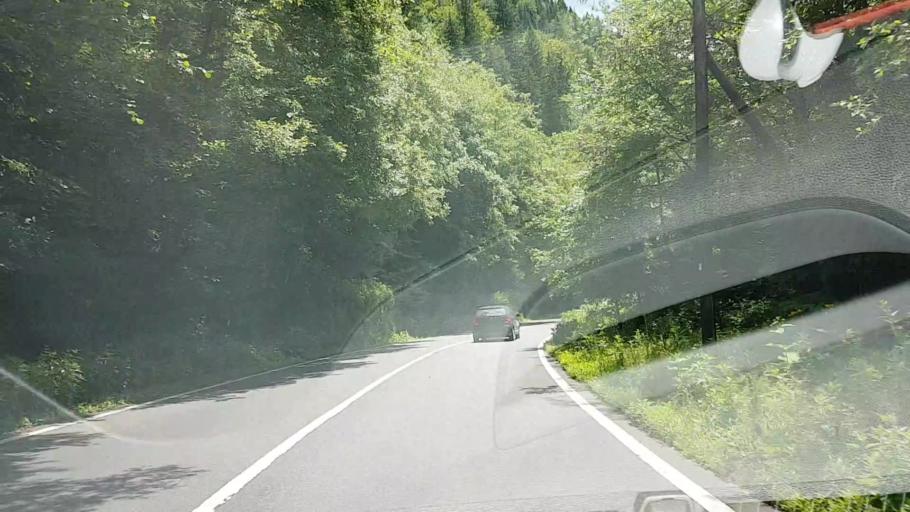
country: RO
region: Suceava
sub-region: Comuna Brosteni
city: Brosteni
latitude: 47.2814
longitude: 25.6497
